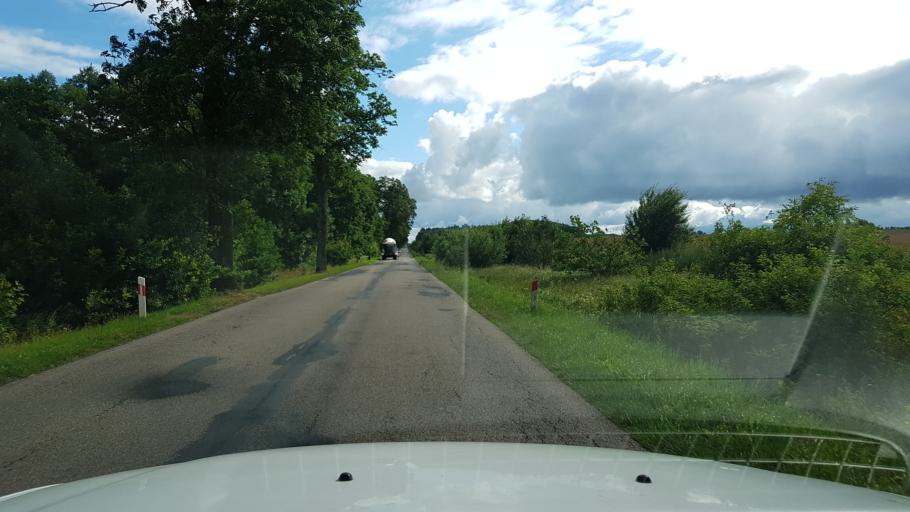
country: PL
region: West Pomeranian Voivodeship
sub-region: Powiat swidwinski
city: Rabino
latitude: 53.7808
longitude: 15.9908
